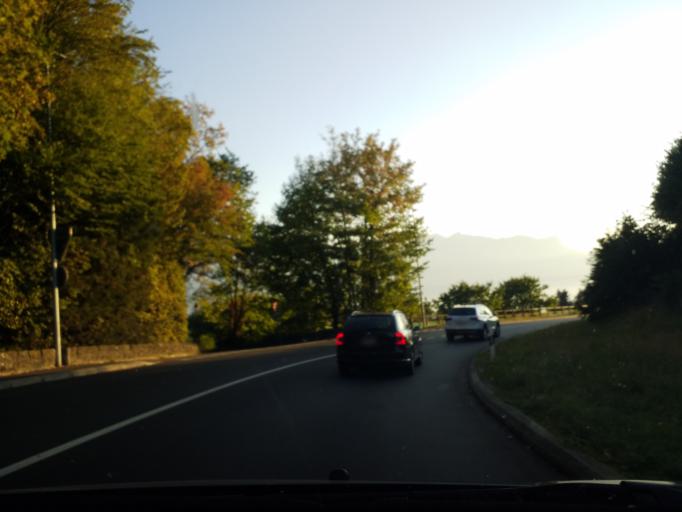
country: CH
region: Vaud
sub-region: Riviera-Pays-d'Enhaut District
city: La Tour-de-Peilz
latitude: 46.4663
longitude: 6.8661
